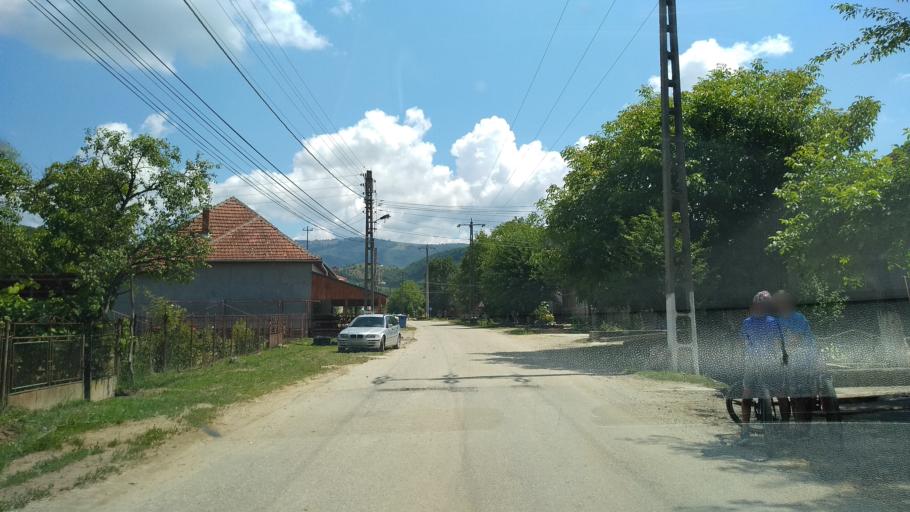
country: RO
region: Hunedoara
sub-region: Comuna Orastioara de Sus
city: Orastioara de Sus
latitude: 45.7114
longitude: 23.1248
